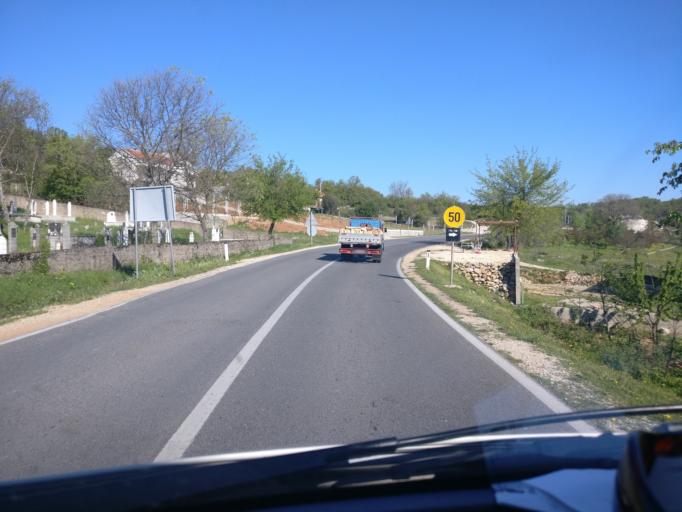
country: BA
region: Federation of Bosnia and Herzegovina
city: Crnici
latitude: 43.1066
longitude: 17.9055
